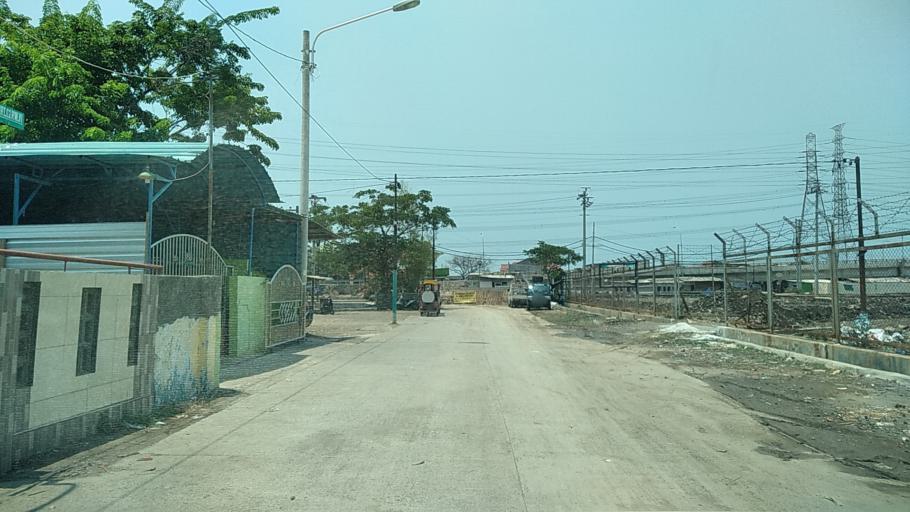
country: ID
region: Central Java
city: Semarang
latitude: -6.9522
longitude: 110.4395
